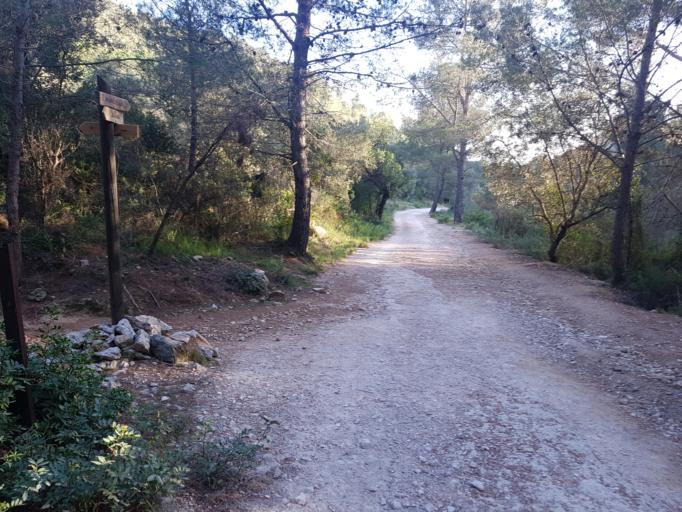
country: ES
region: Andalusia
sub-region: Provincia de Malaga
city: Marbella
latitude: 36.5380
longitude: -4.8839
